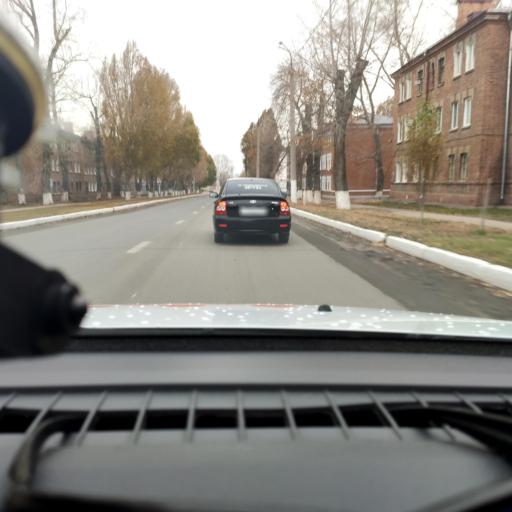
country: RU
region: Samara
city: Chapayevsk
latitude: 52.9794
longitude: 49.7123
